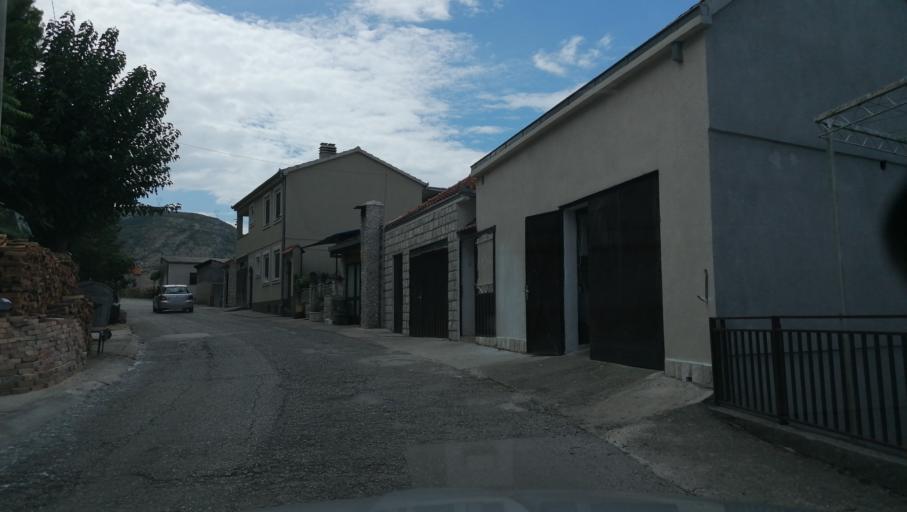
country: BA
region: Republika Srpska
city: Trebinje
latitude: 42.7118
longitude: 18.3572
